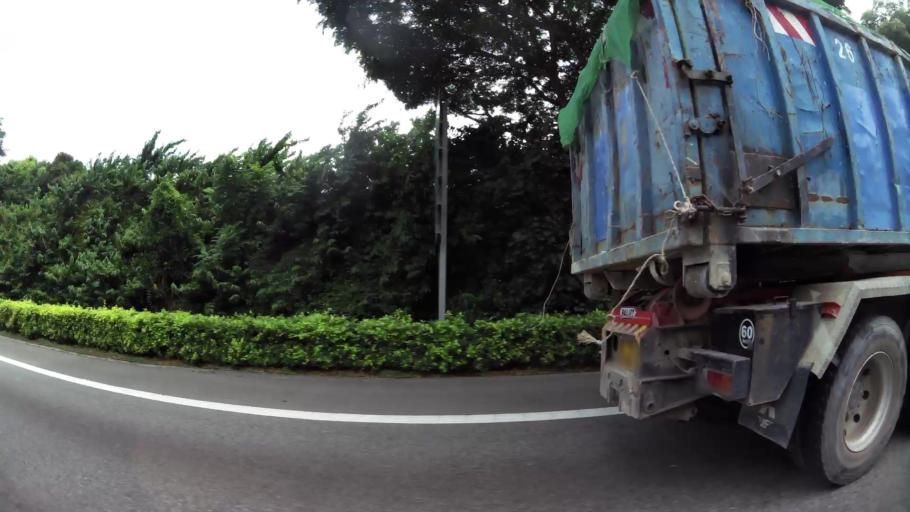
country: MY
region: Johor
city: Kampung Pasir Gudang Baru
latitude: 1.3826
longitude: 103.8585
